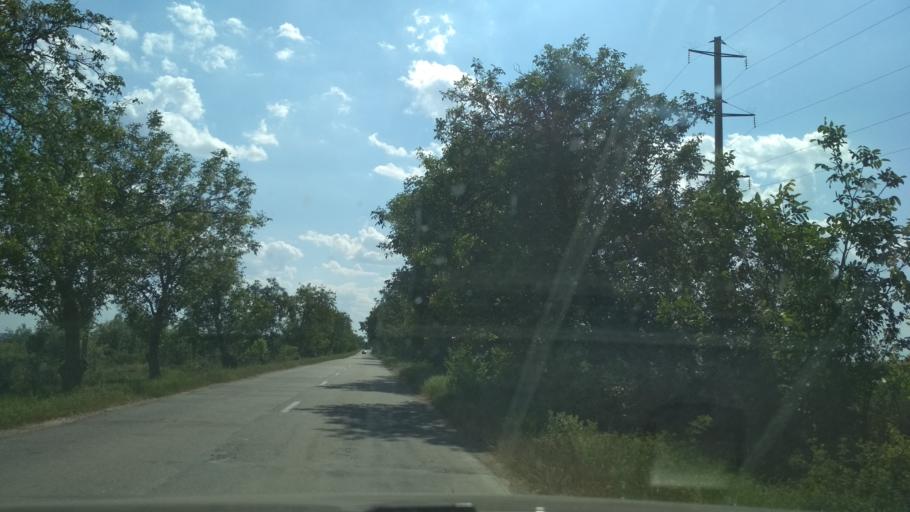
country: MD
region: Criuleni
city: Criuleni
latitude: 47.1665
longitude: 29.1783
